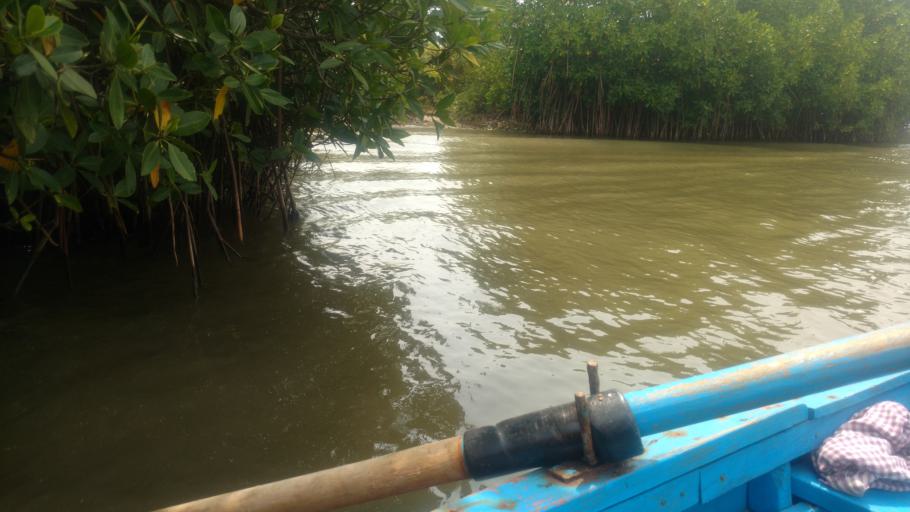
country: IN
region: Tamil Nadu
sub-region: Cuddalore
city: Annamalainagar
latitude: 11.4310
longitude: 79.7918
